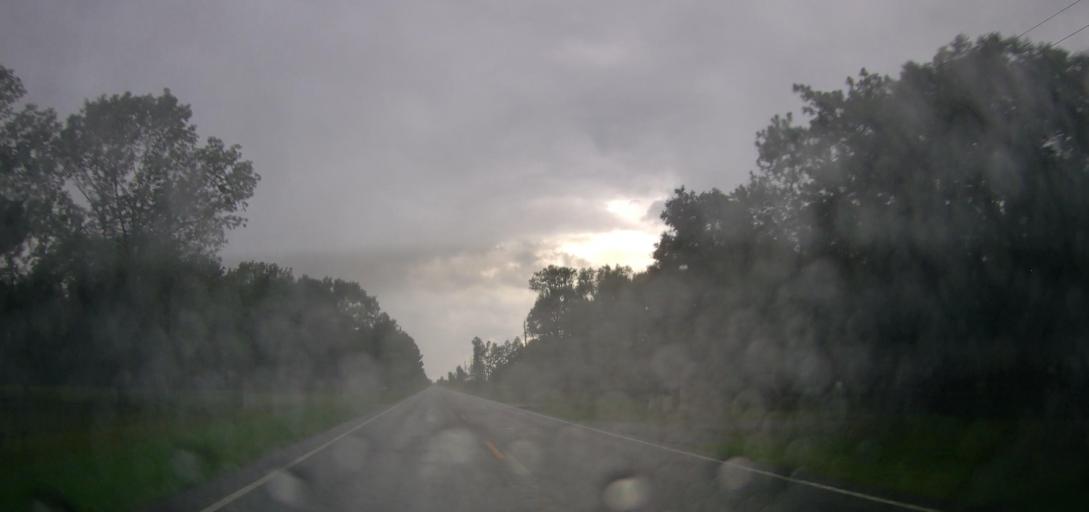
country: US
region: Georgia
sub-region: Brantley County
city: Nahunta
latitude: 31.3325
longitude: -81.7735
